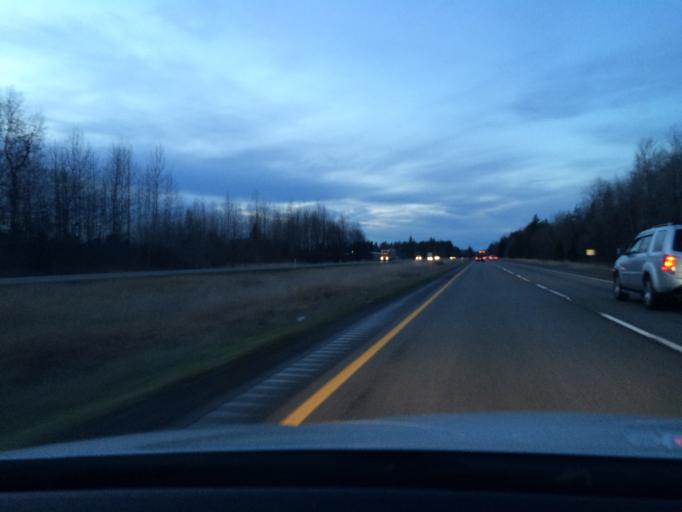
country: US
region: Washington
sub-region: Whatcom County
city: Birch Bay
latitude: 48.9441
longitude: -122.6755
